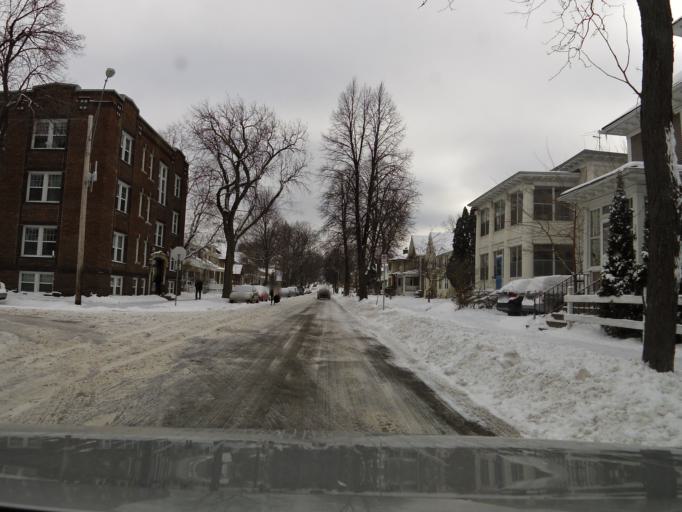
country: US
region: Minnesota
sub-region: Hennepin County
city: Saint Louis Park
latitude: 44.9431
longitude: -93.3009
